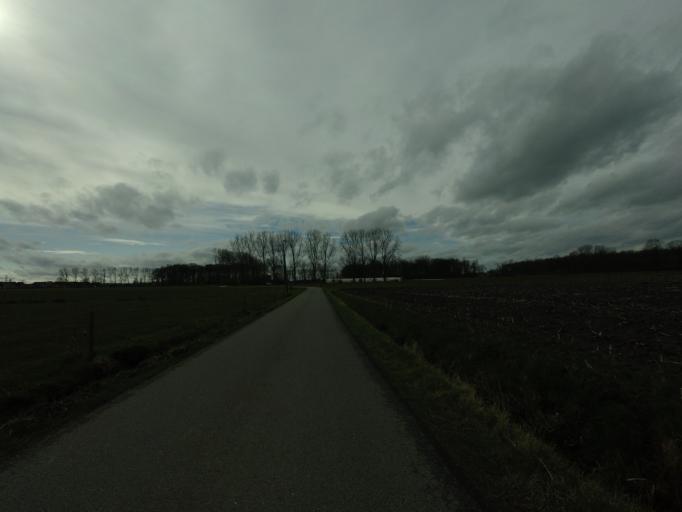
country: BE
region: Flanders
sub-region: Provincie Antwerpen
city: Schelle
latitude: 51.1306
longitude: 4.3594
